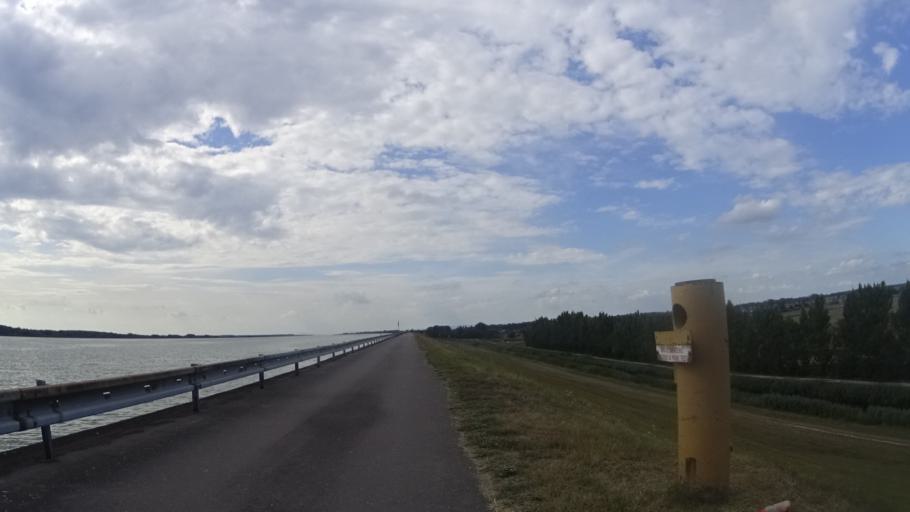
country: SK
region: Trnavsky
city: Gabcikovo
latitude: 47.8933
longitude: 17.5298
